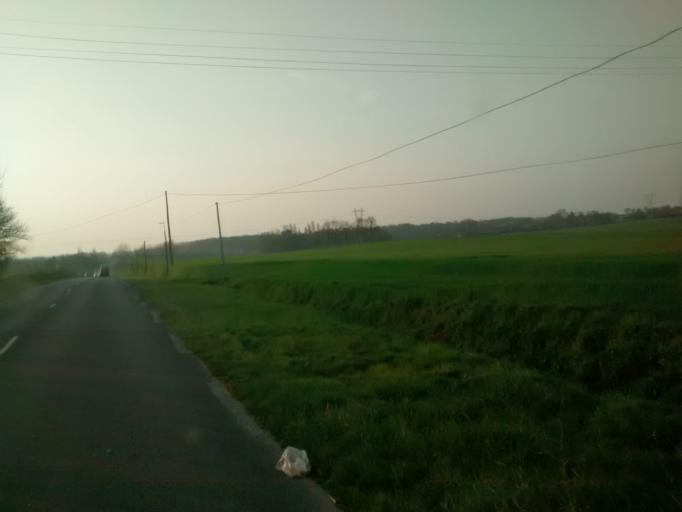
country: FR
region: Brittany
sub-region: Departement d'Ille-et-Vilaine
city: Chavagne
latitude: 48.0632
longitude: -1.8117
